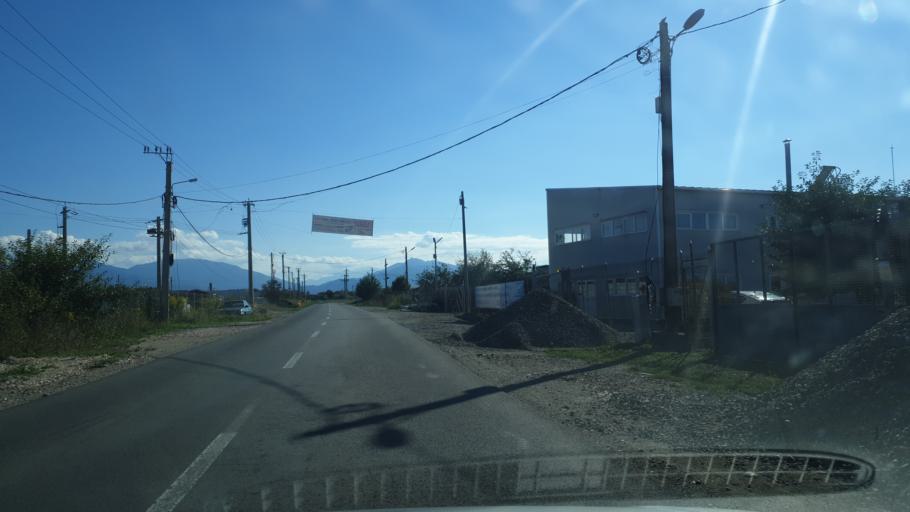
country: RO
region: Brasov
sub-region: Comuna Harman
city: Harman
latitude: 45.7249
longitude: 25.6981
